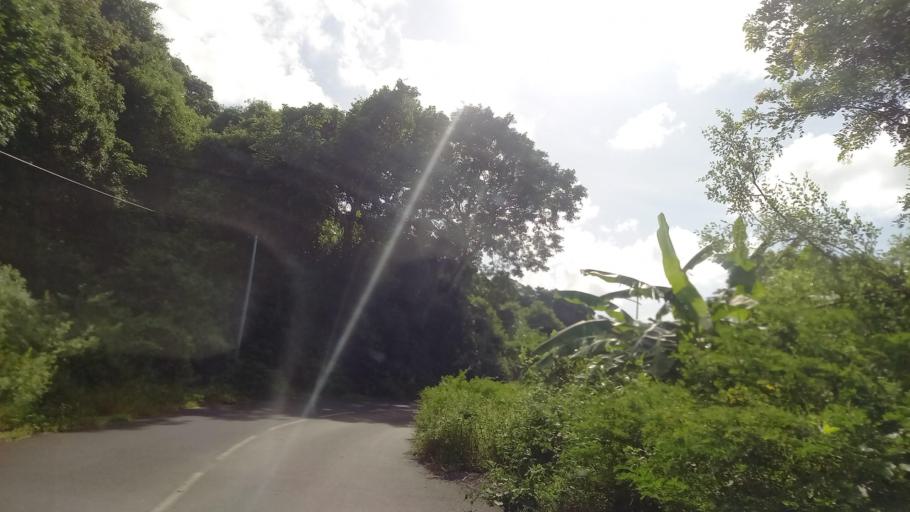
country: YT
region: Kani-Keli
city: Kani Keli
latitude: -12.9883
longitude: 45.1304
